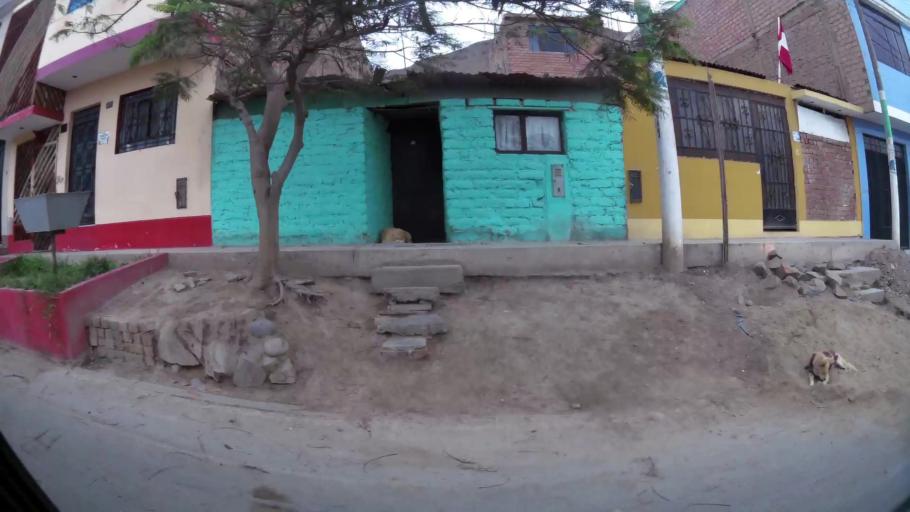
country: PE
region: Lima
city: Ventanilla
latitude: -11.9303
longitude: -77.0853
